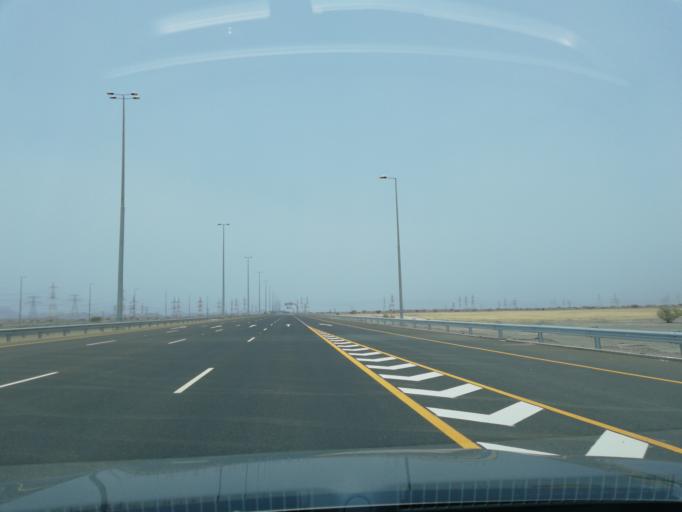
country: OM
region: Al Batinah
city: Al Liwa'
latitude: 24.4093
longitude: 56.5387
